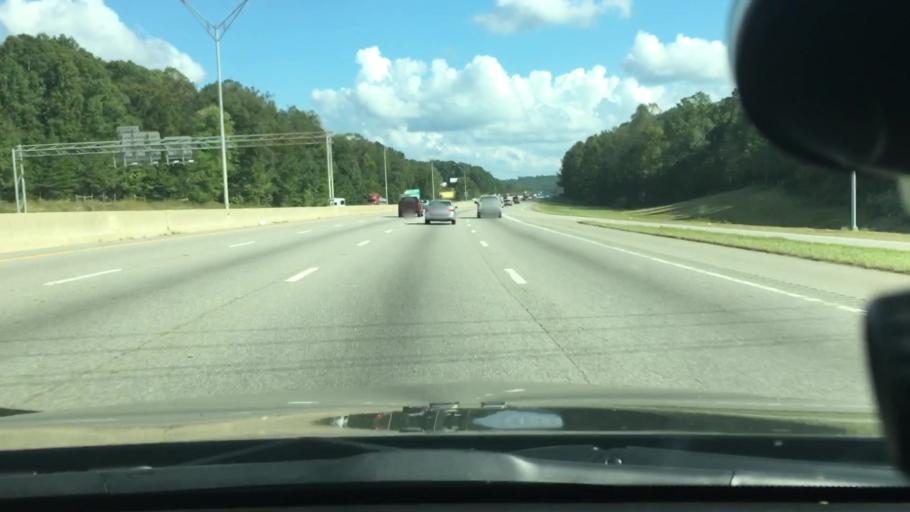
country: US
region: North Carolina
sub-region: Orange County
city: Hillsborough
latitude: 36.0720
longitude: -79.1573
